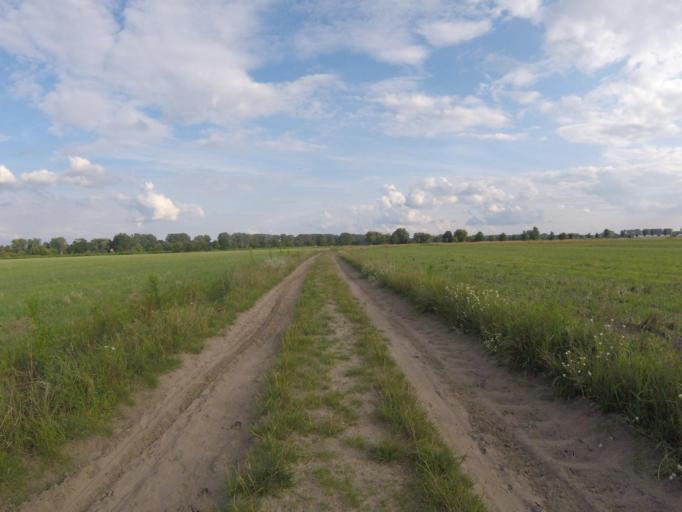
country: DE
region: Brandenburg
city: Mittenwalde
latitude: 52.2811
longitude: 13.5550
